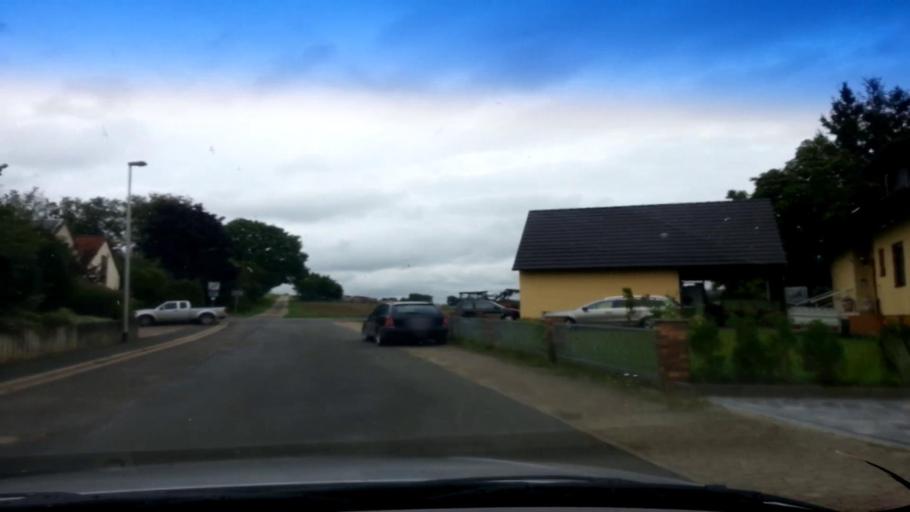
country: DE
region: Bavaria
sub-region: Upper Franconia
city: Memmelsdorf
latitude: 49.9449
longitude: 10.9763
